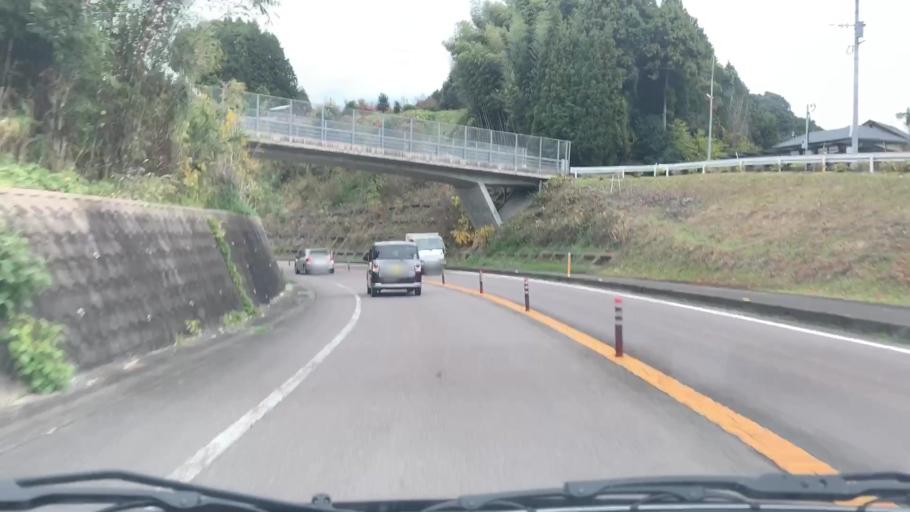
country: JP
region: Saga Prefecture
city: Ureshinomachi-shimojuku
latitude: 33.0879
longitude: 130.0152
